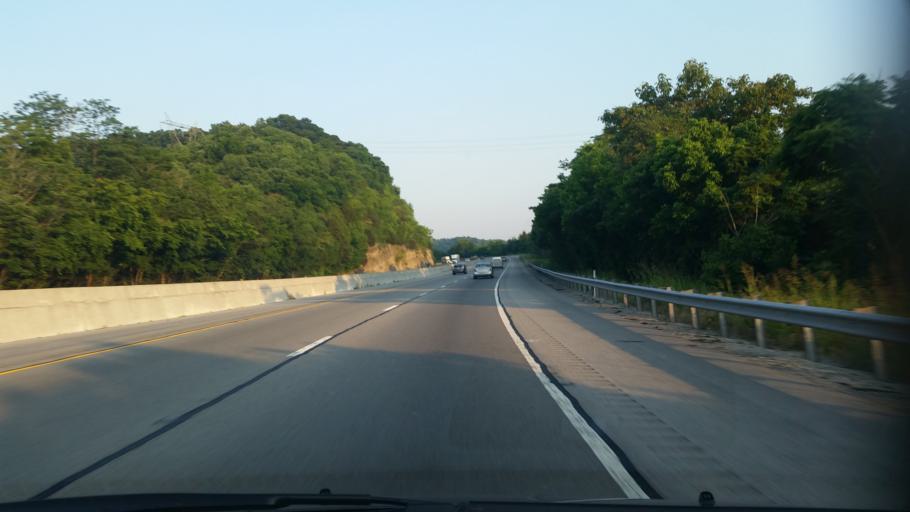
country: US
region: Tennessee
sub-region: Putnam County
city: Lafayette
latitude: 36.1124
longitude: -85.7716
